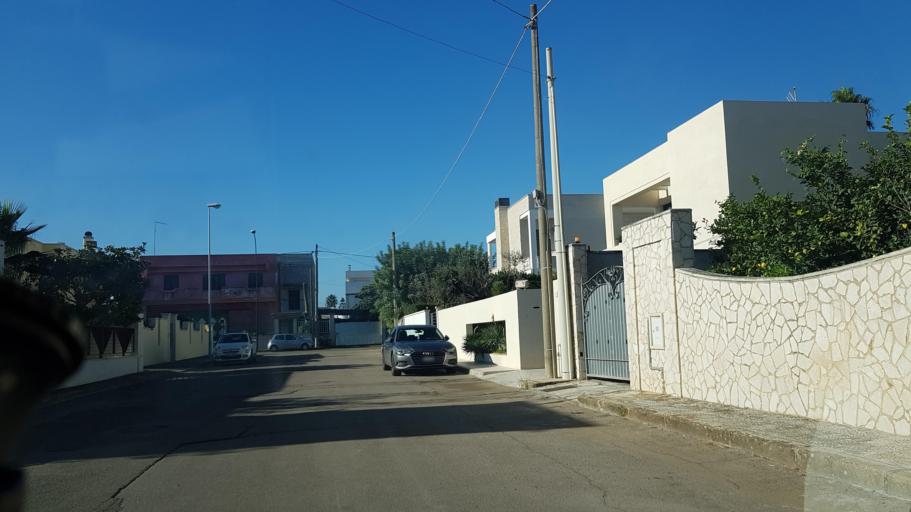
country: IT
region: Apulia
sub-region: Provincia di Lecce
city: Squinzano
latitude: 40.4273
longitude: 18.0419
